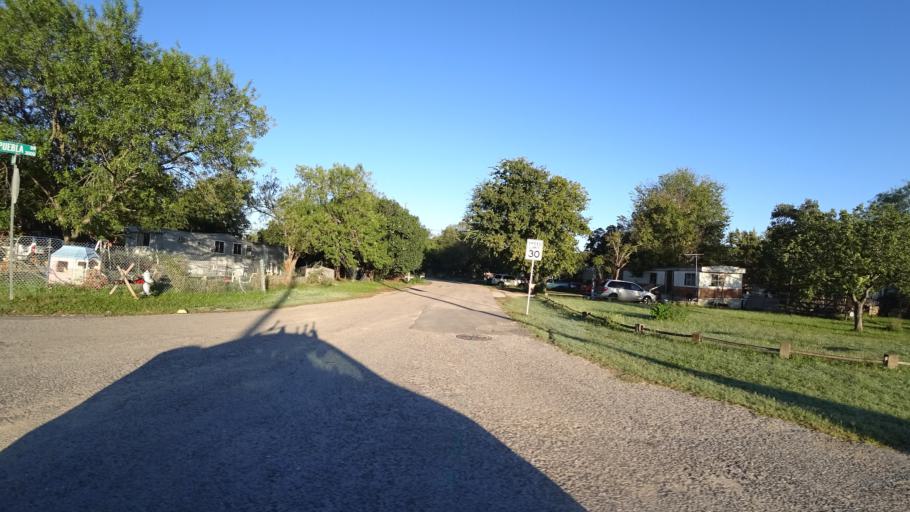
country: US
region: Texas
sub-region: Travis County
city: Hornsby Bend
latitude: 30.2053
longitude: -97.6344
